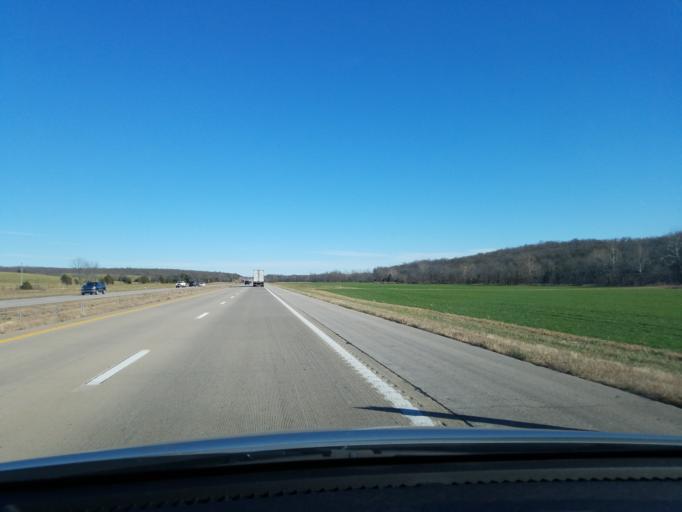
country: US
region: Missouri
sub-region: Laclede County
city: Lebanon
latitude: 37.7526
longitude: -92.5669
